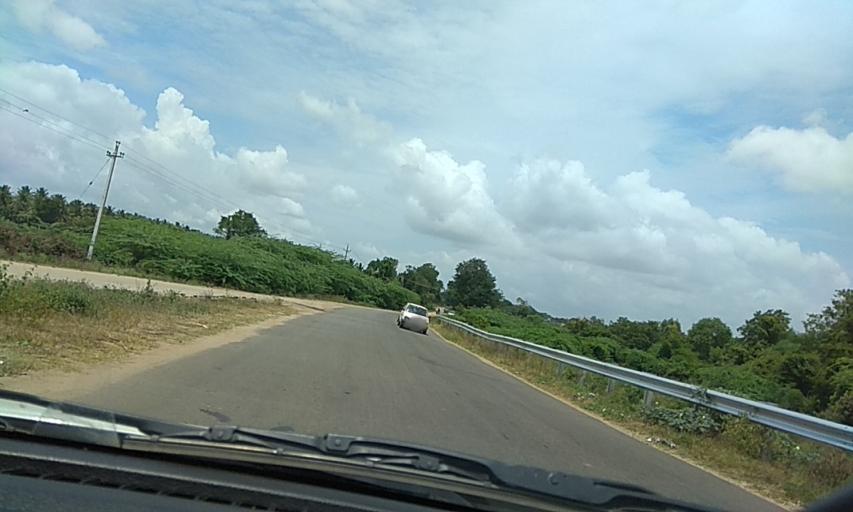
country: IN
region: Karnataka
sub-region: Chamrajnagar
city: Gundlupet
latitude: 11.8108
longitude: 76.7256
